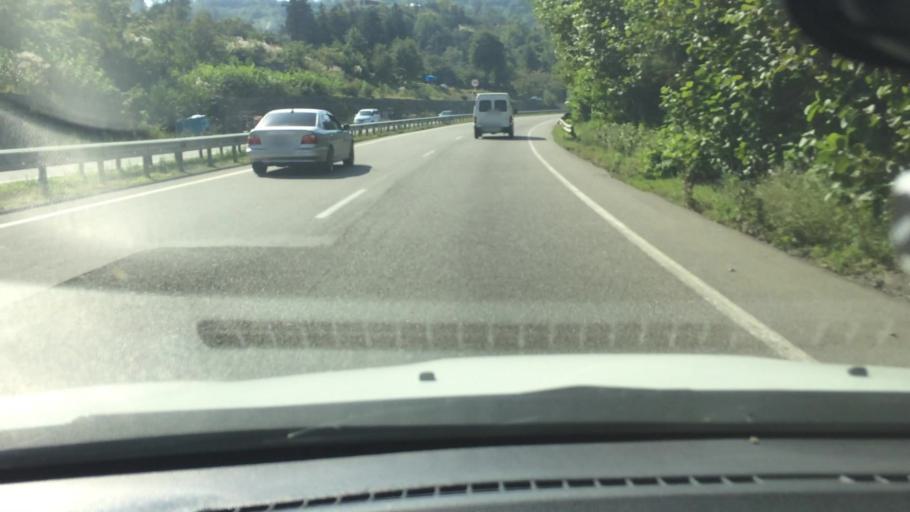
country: GE
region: Ajaria
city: Makhinjauri
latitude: 41.6962
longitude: 41.7271
